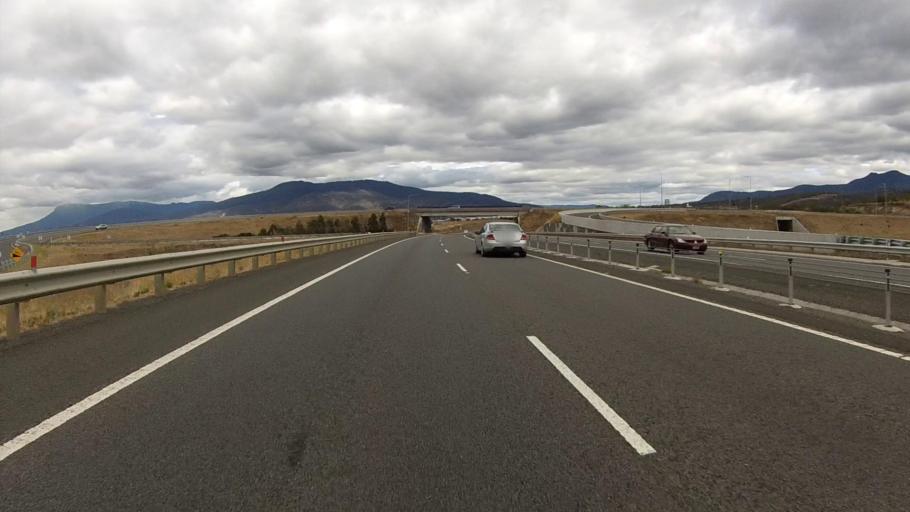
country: AU
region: Tasmania
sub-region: Brighton
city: Bridgewater
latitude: -42.7127
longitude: 147.2470
